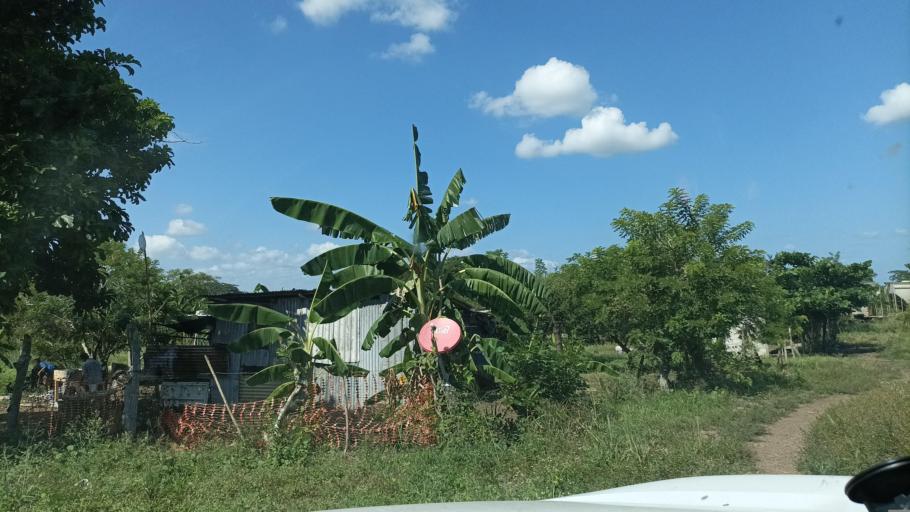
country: MX
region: Veracruz
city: Manlio Fabio Altamirano
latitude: 19.0872
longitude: -96.3435
